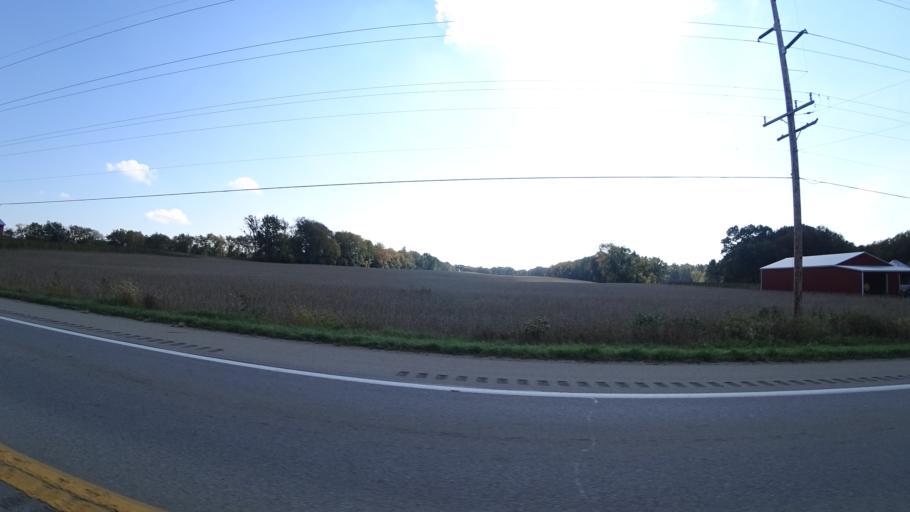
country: US
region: Michigan
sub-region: Jackson County
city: Concord
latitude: 42.1644
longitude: -84.6817
